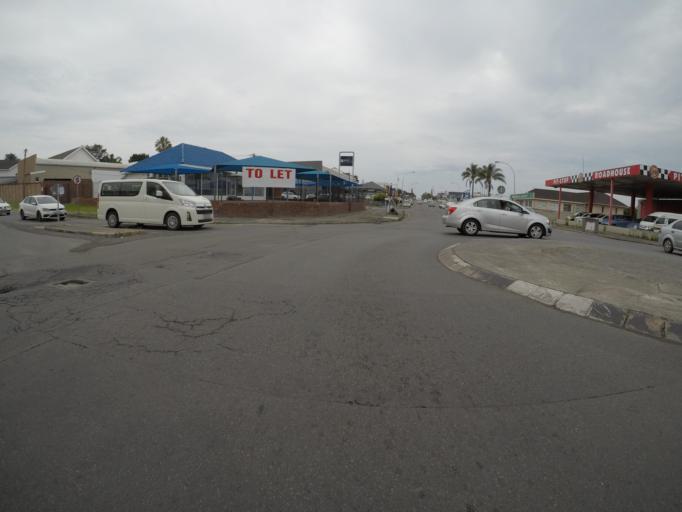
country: ZA
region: Eastern Cape
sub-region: Buffalo City Metropolitan Municipality
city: East London
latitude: -32.9844
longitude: 27.9049
